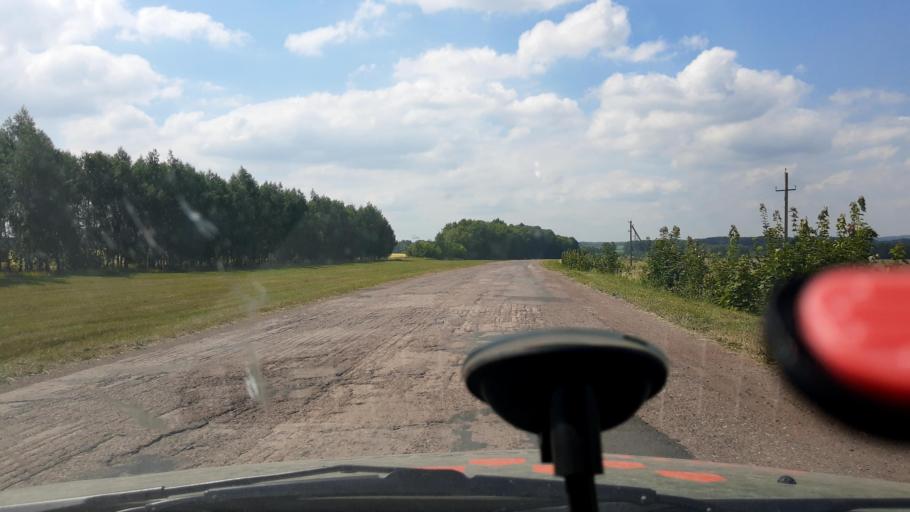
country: RU
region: Bashkortostan
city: Chekmagush
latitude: 54.8851
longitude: 54.5922
